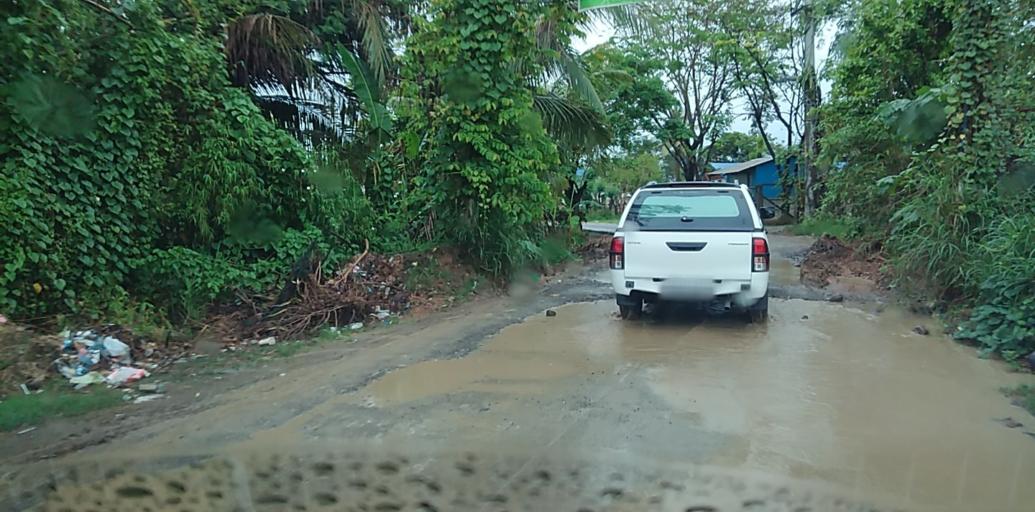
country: PH
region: Central Luzon
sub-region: Province of Pampanga
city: Batasan Bata
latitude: 15.1393
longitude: 120.9436
